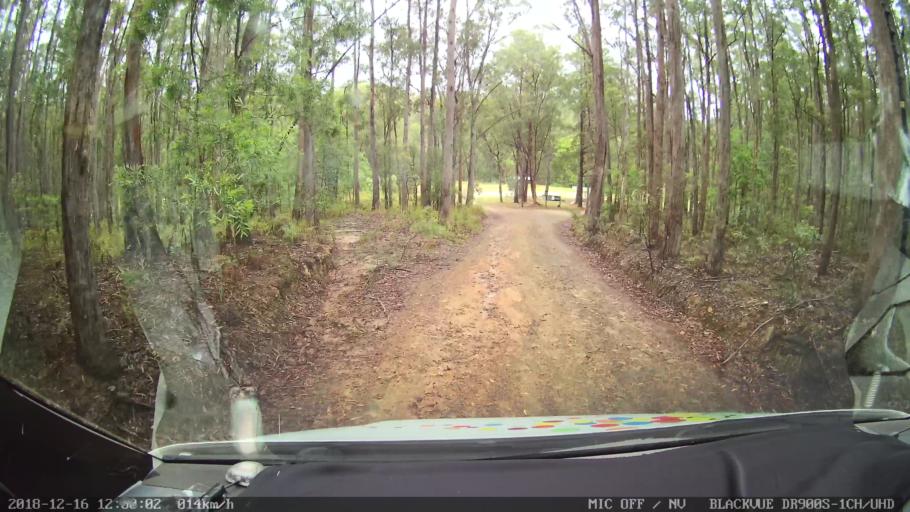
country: AU
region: New South Wales
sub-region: Tenterfield Municipality
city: Carrolls Creek
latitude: -28.9269
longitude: 152.3139
